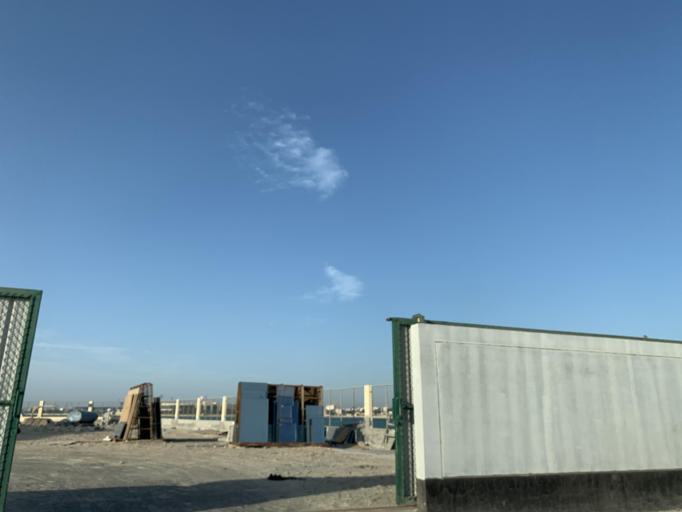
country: BH
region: Muharraq
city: Al Muharraq
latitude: 26.2469
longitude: 50.6214
